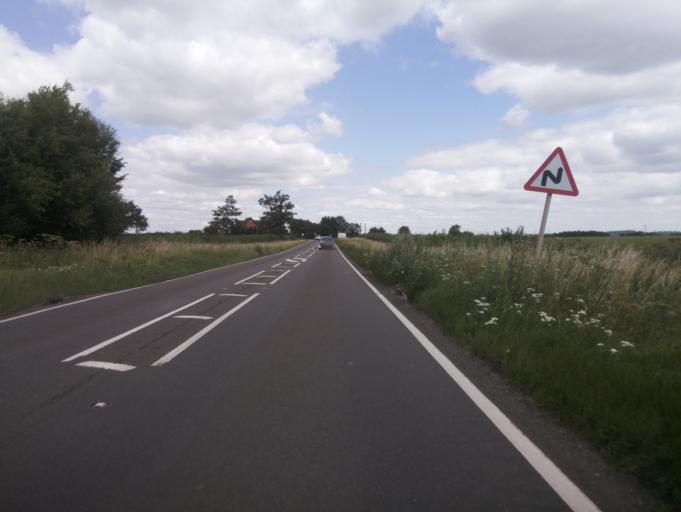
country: GB
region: England
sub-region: Buckinghamshire
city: Winslow
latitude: 51.9108
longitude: -0.8385
